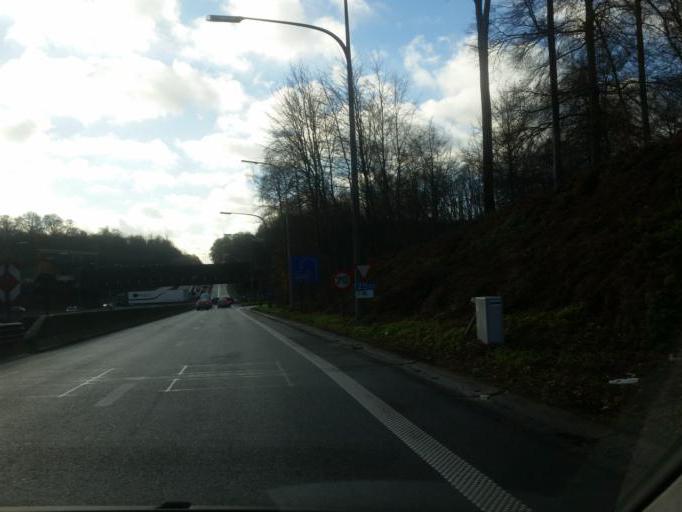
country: BE
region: Flanders
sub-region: Provincie Vlaams-Brabant
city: Hoeilaart
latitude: 50.7702
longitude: 4.4447
